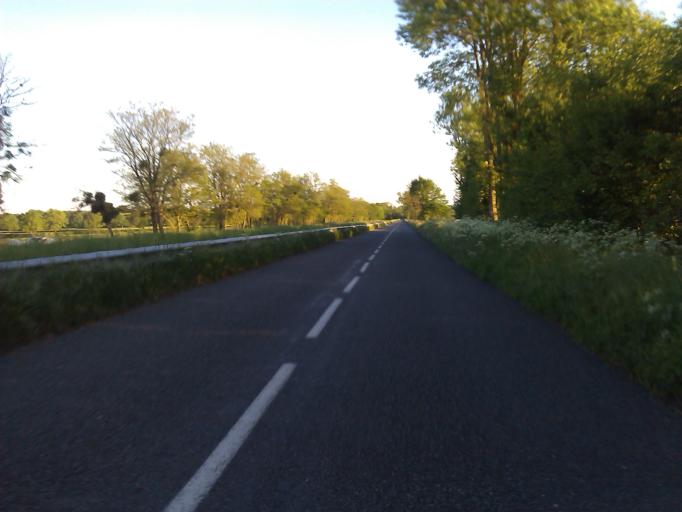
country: FR
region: Bourgogne
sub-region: Departement de Saone-et-Loire
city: Palinges
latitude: 46.4990
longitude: 4.1839
